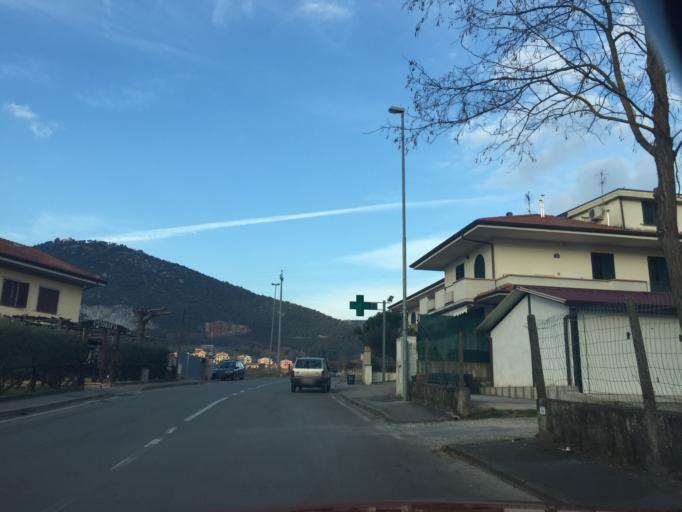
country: IT
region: Tuscany
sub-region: Provincia di Pistoia
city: Monsummano Terme
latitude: 43.8605
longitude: 10.8249
